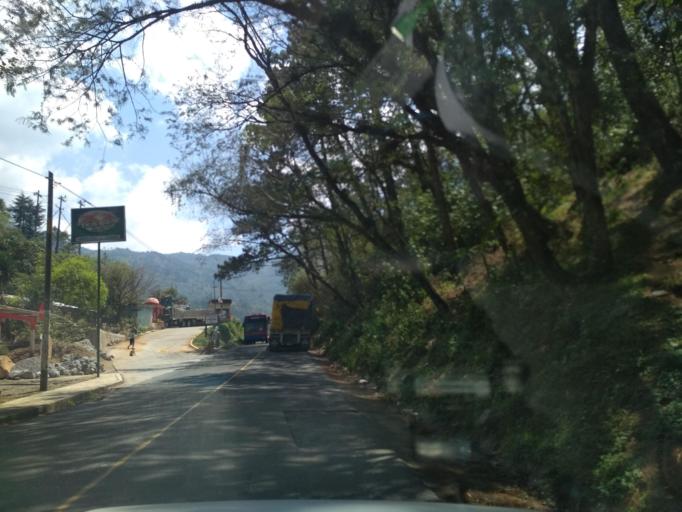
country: MX
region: Veracruz
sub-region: Tlilapan
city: Tonalixco
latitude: 18.7776
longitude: -97.0831
